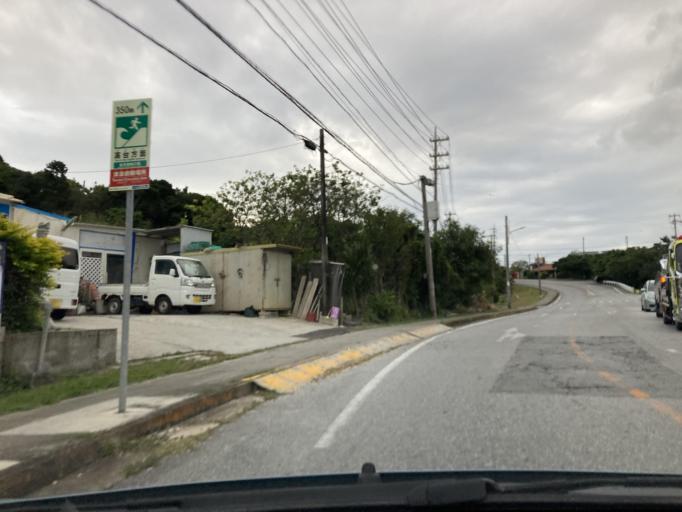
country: JP
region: Okinawa
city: Ginowan
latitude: 26.2792
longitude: 127.7486
